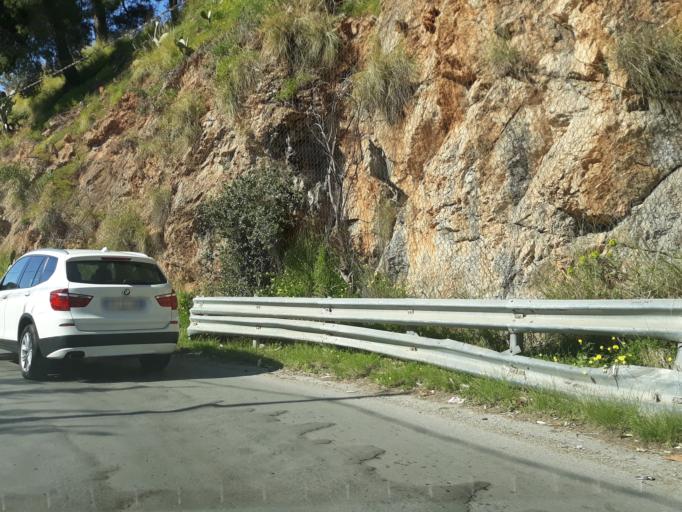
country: IT
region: Sicily
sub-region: Palermo
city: Monreale
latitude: 38.0942
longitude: 13.3061
